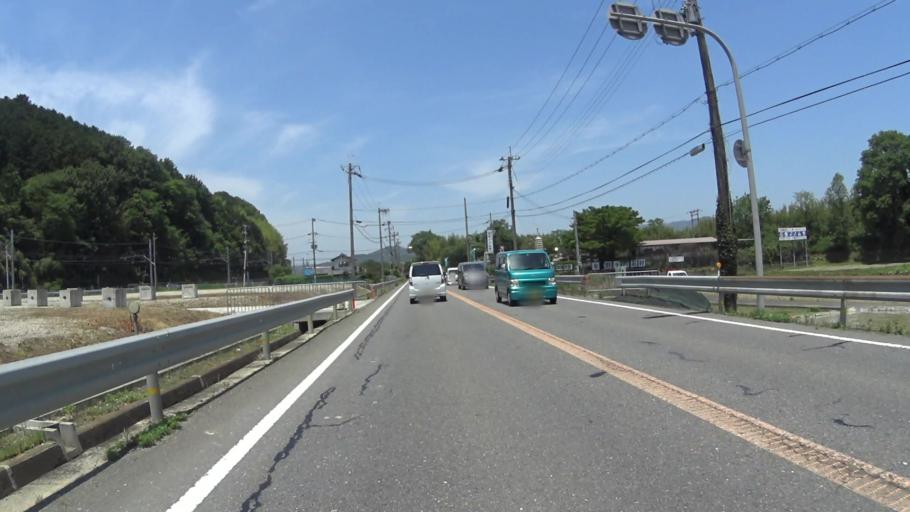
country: JP
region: Kyoto
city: Kameoka
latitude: 35.0601
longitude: 135.5463
